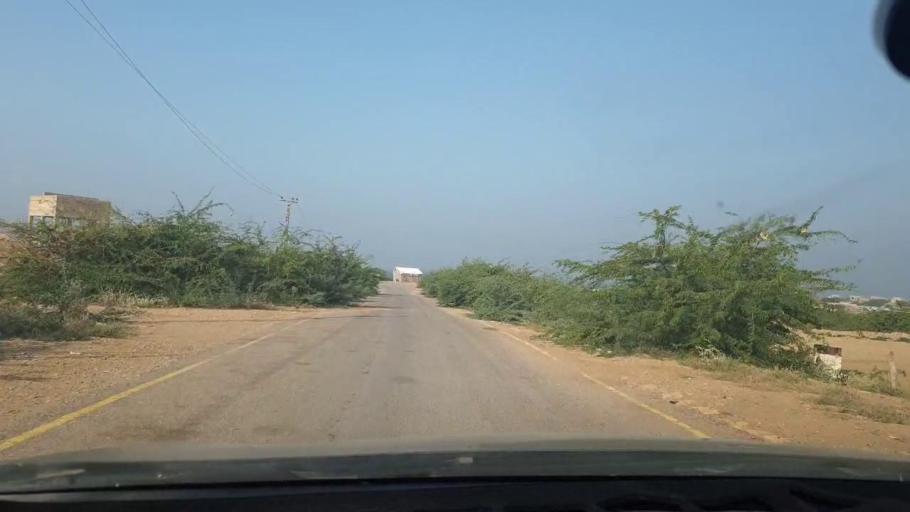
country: PK
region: Balochistan
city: Gadani
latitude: 24.8488
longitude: 66.6645
